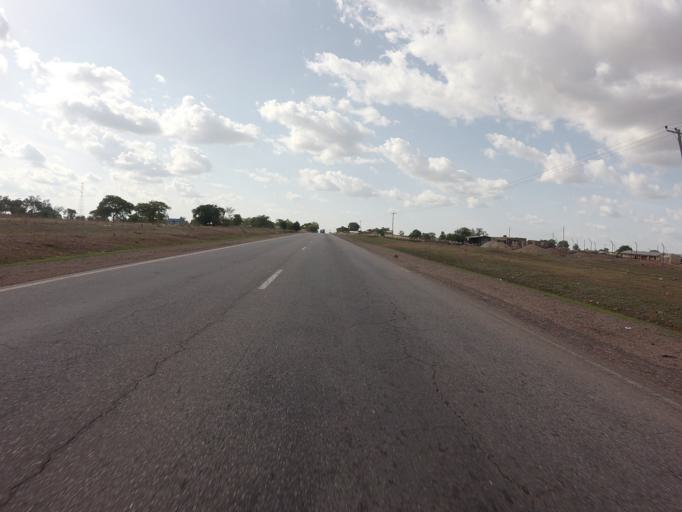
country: GH
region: Upper East
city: Bolgatanga
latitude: 10.6746
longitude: -0.8612
